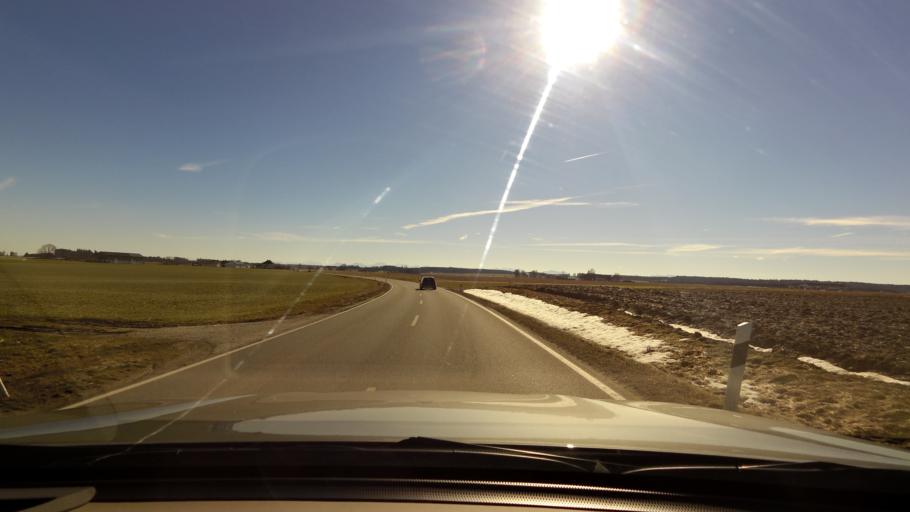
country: DE
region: Bavaria
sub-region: Upper Bavaria
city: Kraiburg am Inn
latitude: 48.1798
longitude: 12.4547
